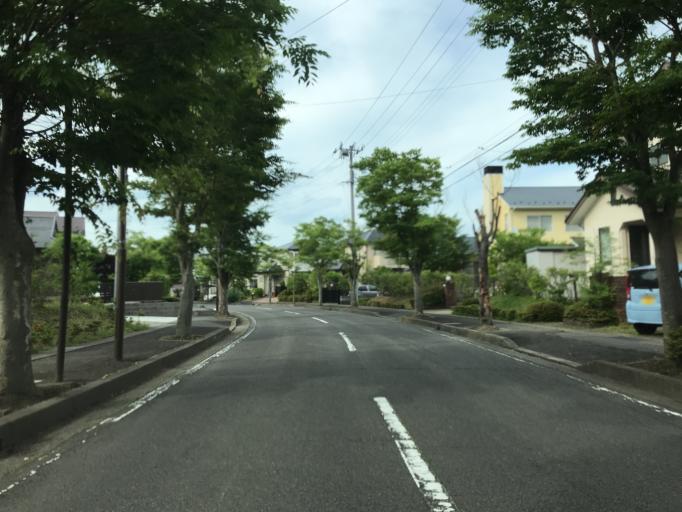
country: JP
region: Fukushima
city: Nihommatsu
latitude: 37.6620
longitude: 140.4705
